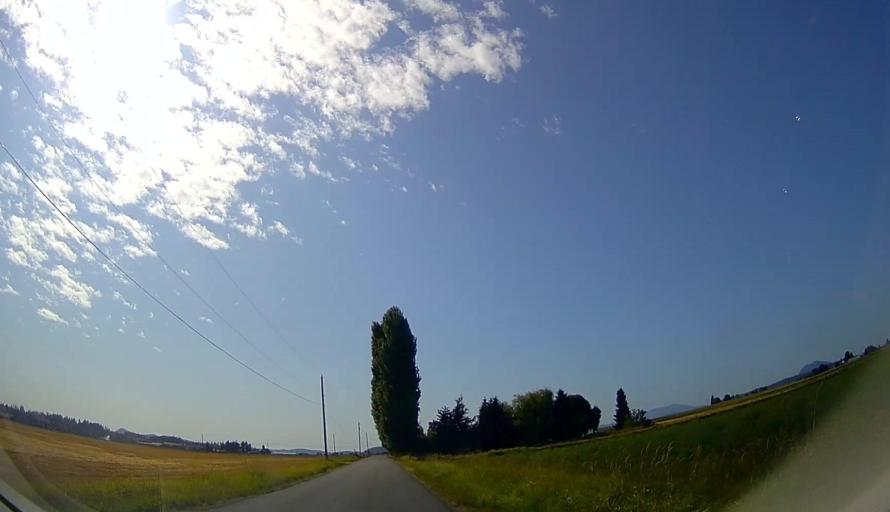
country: US
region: Washington
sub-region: Skagit County
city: Burlington
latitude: 48.5233
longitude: -122.4407
